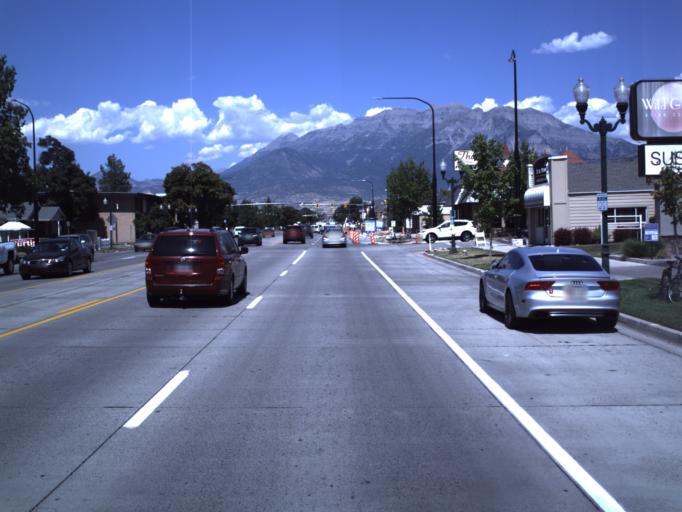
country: US
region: Utah
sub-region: Utah County
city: Provo
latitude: 40.2385
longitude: -111.6586
